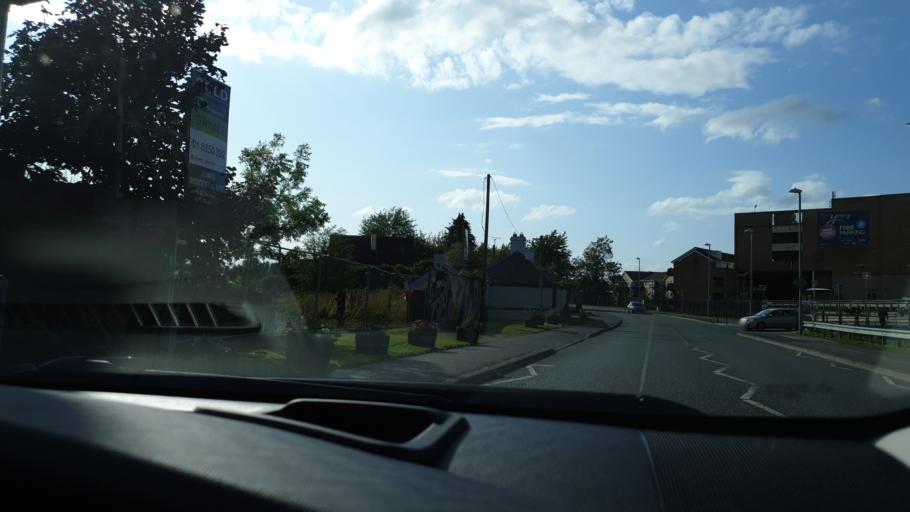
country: IE
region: Leinster
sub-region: An Mhi
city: Ashbourne
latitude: 53.5094
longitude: -6.3982
